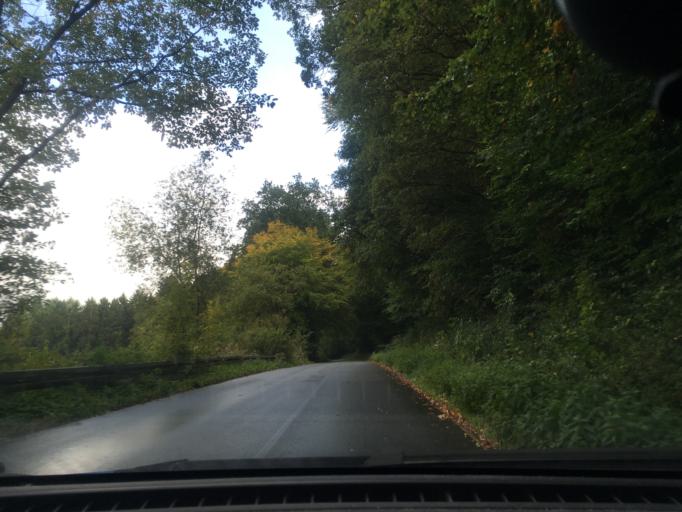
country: DE
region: Lower Saxony
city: Bodenfelde
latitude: 51.6201
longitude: 9.5780
